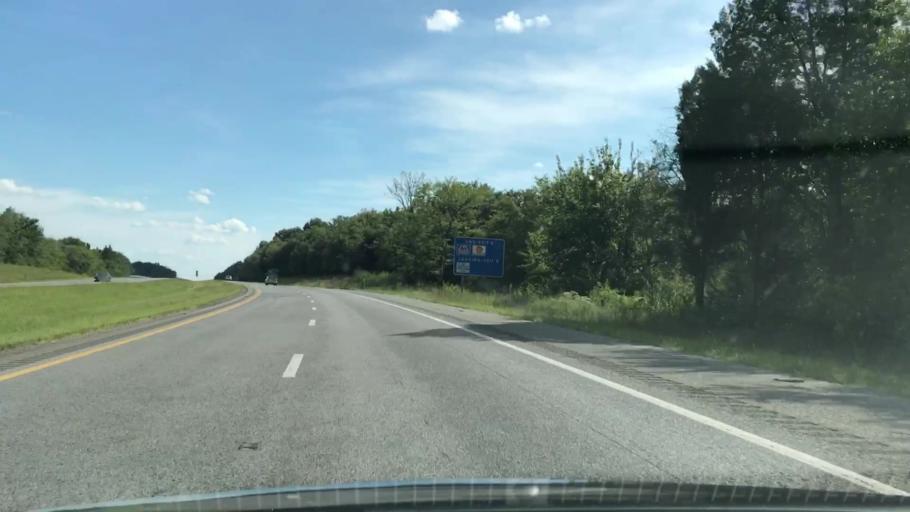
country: US
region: Alabama
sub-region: Limestone County
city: Ardmore
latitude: 35.1047
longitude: -86.8859
